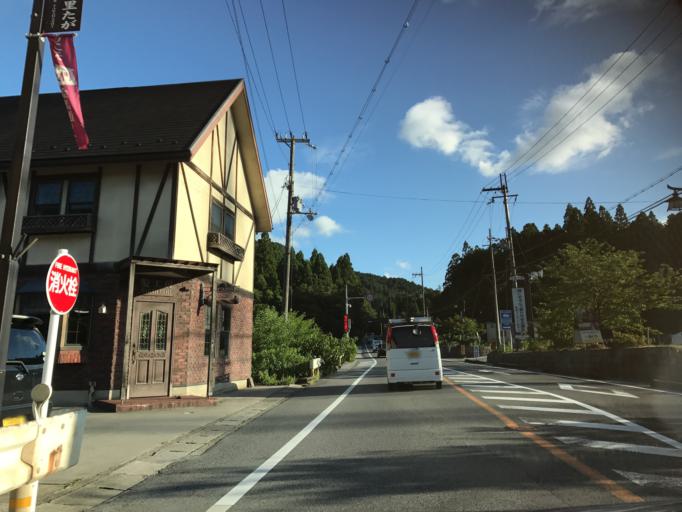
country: JP
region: Shiga Prefecture
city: Hikone
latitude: 35.2221
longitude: 136.2917
